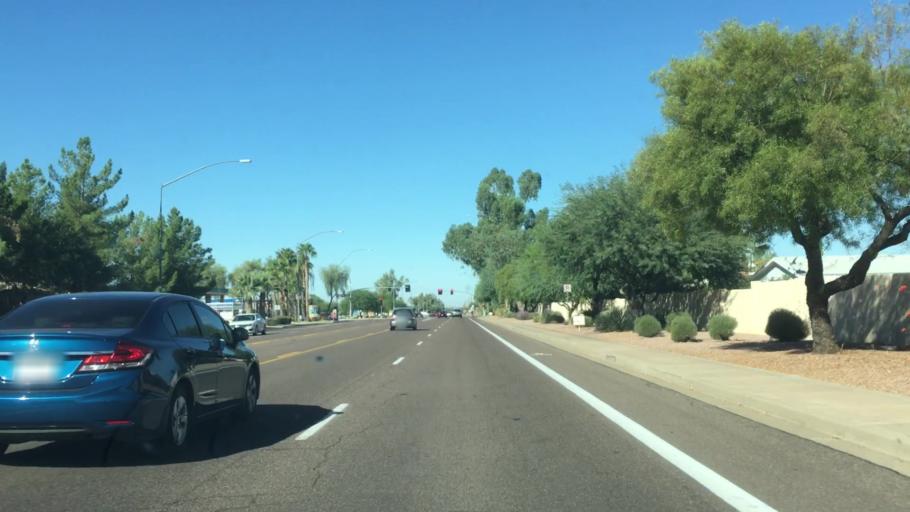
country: US
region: Arizona
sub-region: Maricopa County
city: Mesa
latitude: 33.4519
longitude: -111.7167
